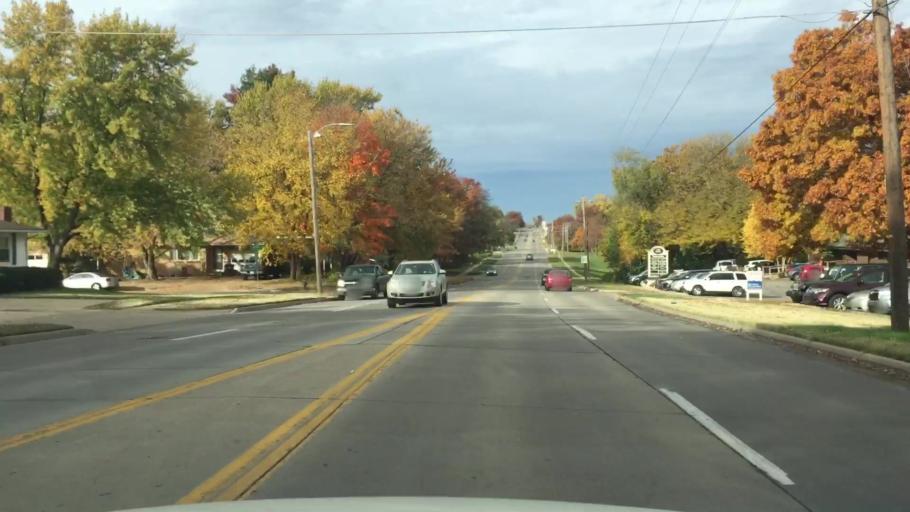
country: US
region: Kansas
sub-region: Shawnee County
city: Topeka
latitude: 39.0152
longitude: -95.7073
